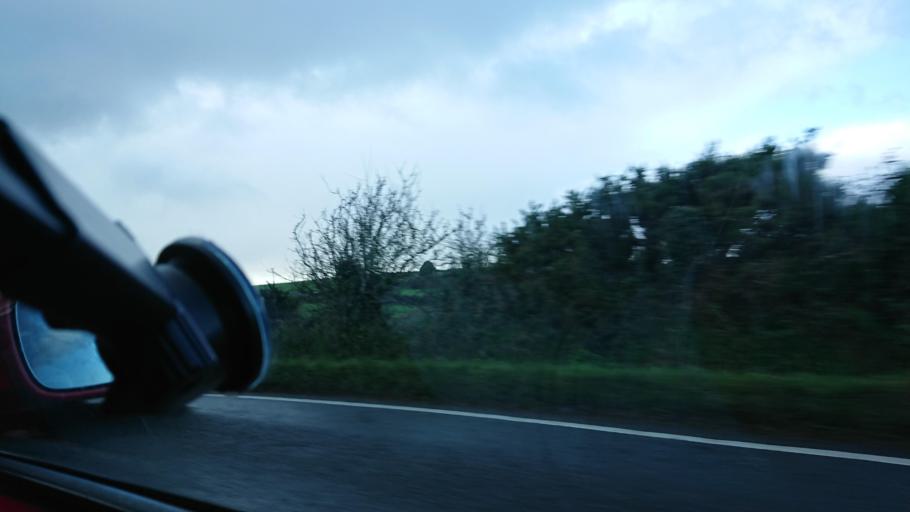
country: GB
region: England
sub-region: Cornwall
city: Looe
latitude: 50.3499
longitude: -4.4771
